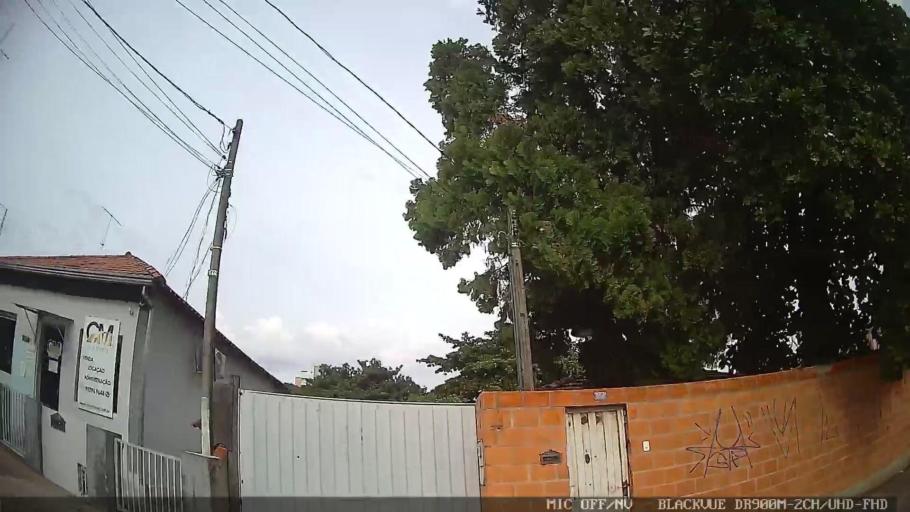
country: BR
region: Sao Paulo
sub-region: Indaiatuba
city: Indaiatuba
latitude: -23.0848
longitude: -47.2176
